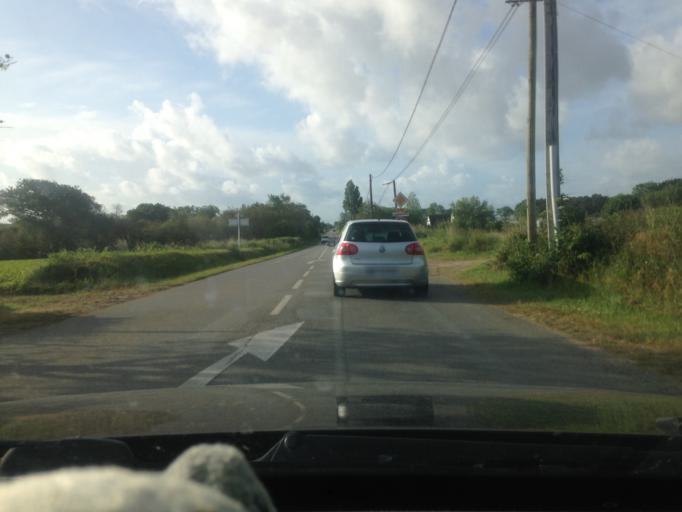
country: FR
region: Brittany
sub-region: Departement du Morbihan
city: Erdeven
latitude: 47.6344
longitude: -3.1489
